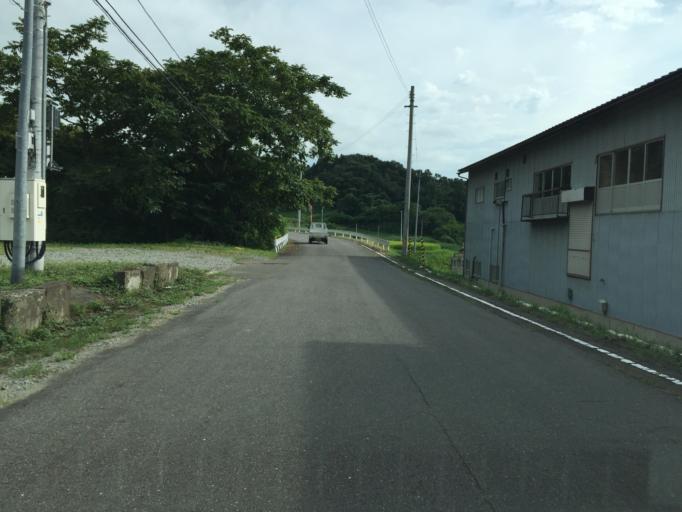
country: JP
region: Fukushima
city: Fukushima-shi
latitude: 37.6921
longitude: 140.5250
